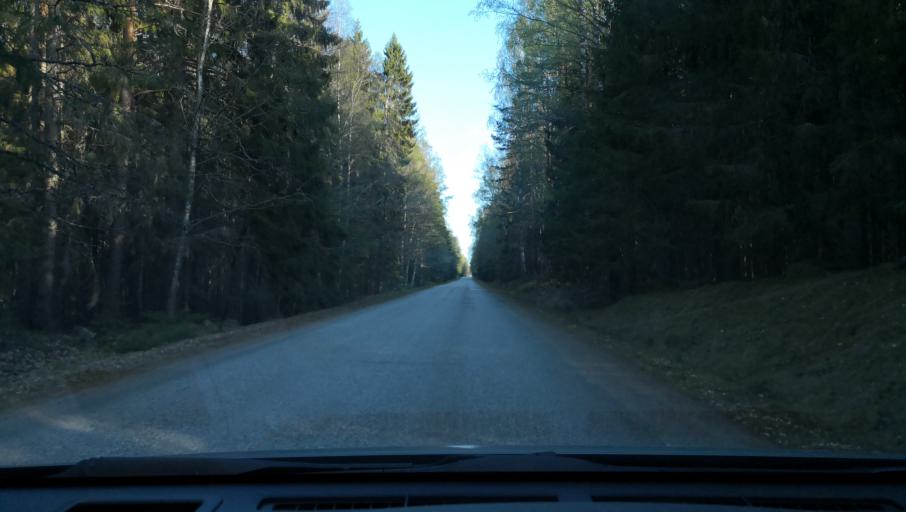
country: SE
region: Uppsala
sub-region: Heby Kommun
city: Tarnsjo
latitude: 60.2774
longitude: 16.8941
